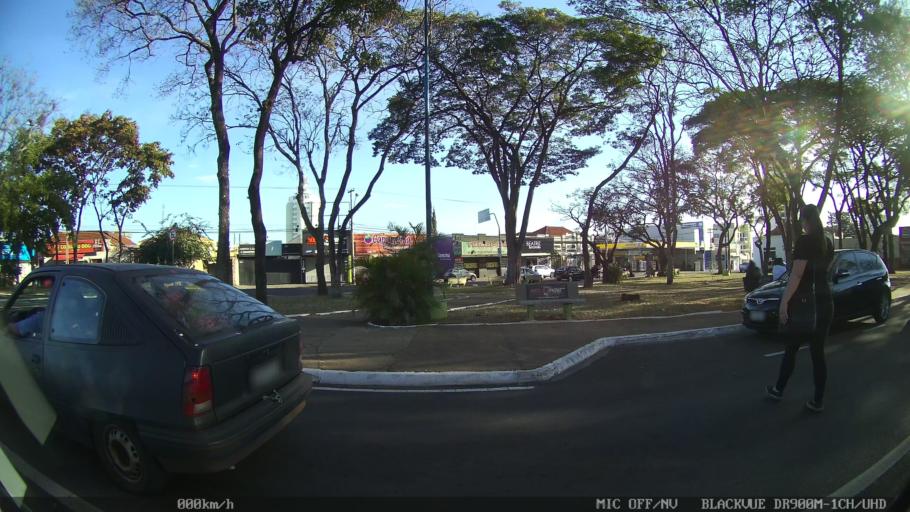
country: BR
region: Sao Paulo
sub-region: Franca
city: Franca
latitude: -20.5324
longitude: -47.3970
